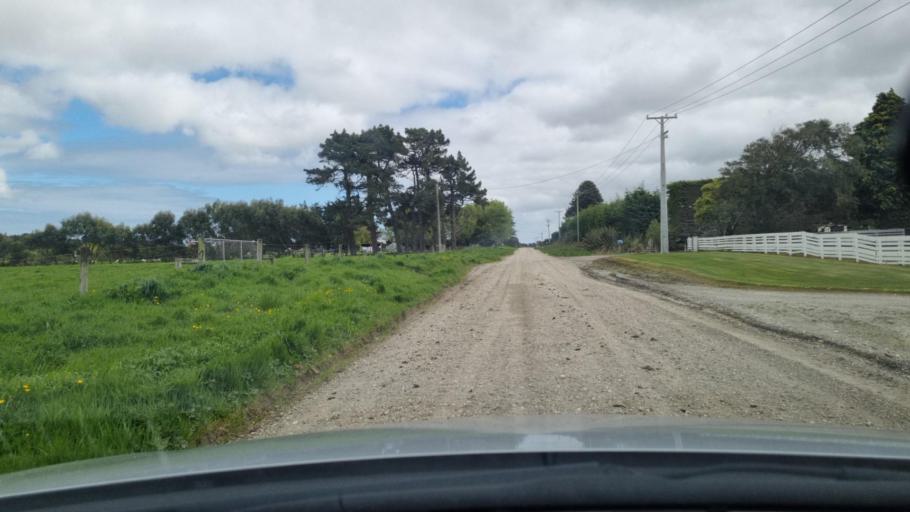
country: NZ
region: Southland
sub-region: Invercargill City
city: Invercargill
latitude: -46.4433
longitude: 168.4085
